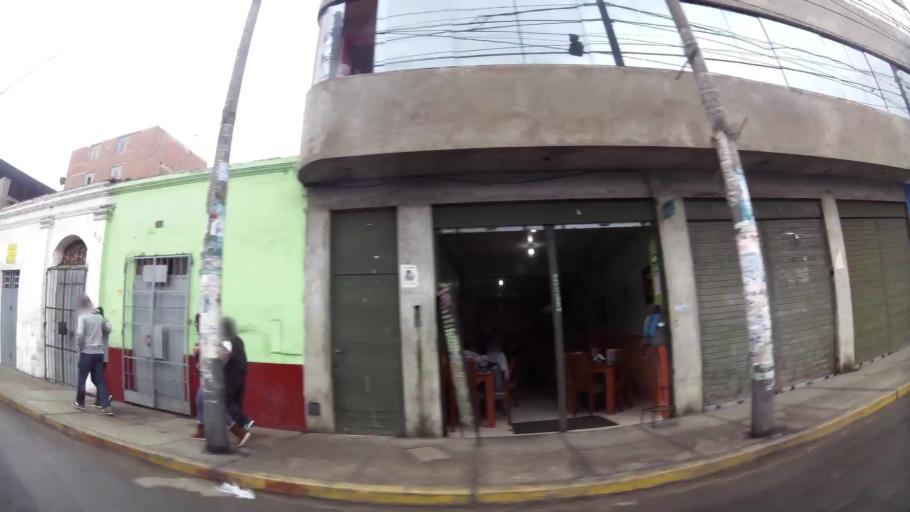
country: PE
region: Lima
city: Lima
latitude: -12.0604
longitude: -77.0231
